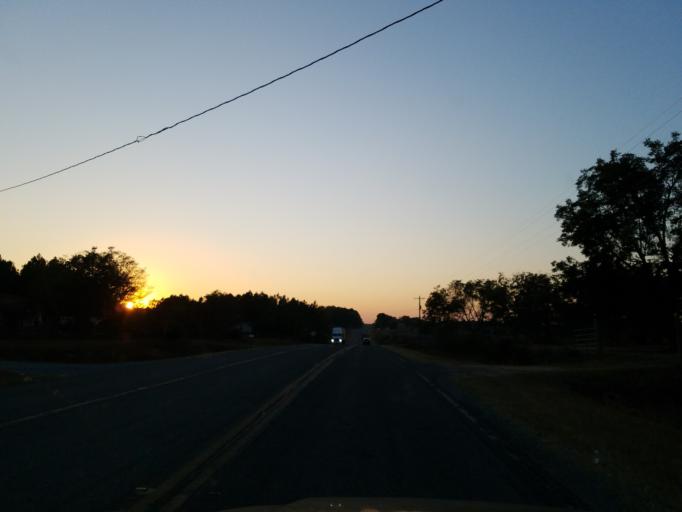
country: US
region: Georgia
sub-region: Ben Hill County
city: Fitzgerald
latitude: 31.7199
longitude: -83.3946
